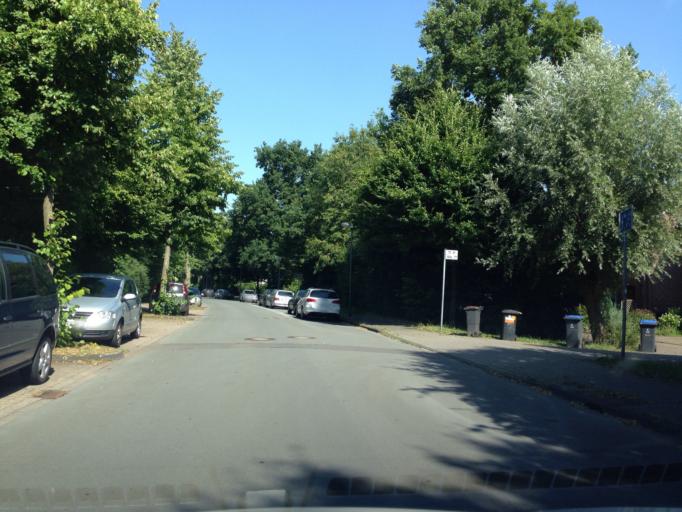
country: DE
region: North Rhine-Westphalia
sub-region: Regierungsbezirk Munster
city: Muenster
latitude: 51.9714
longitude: 7.5611
